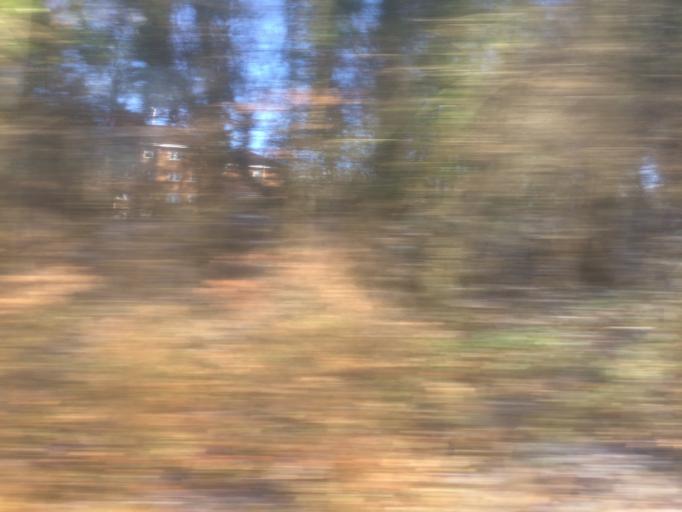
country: GB
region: Scotland
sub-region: East Renfrewshire
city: Clarkston
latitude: 55.8003
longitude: -4.2799
